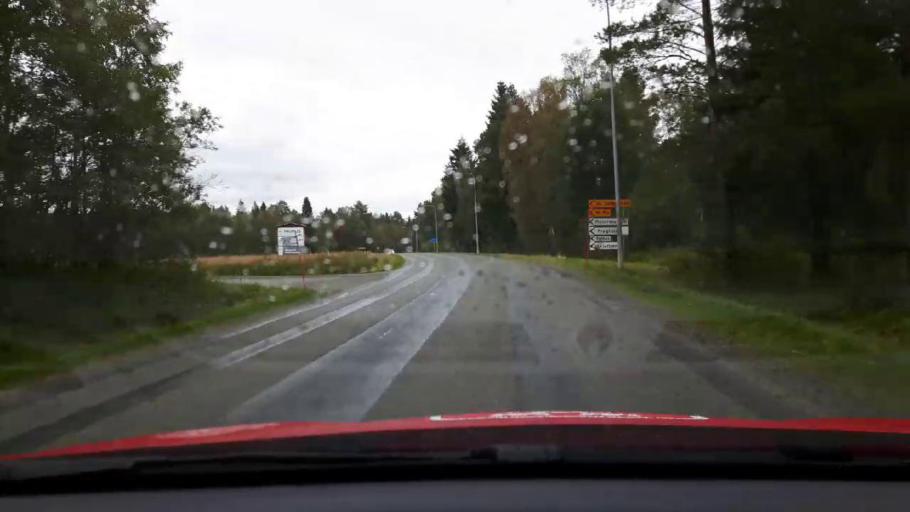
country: SE
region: Jaemtland
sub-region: Bergs Kommun
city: Hoverberg
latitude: 62.7727
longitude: 14.4299
